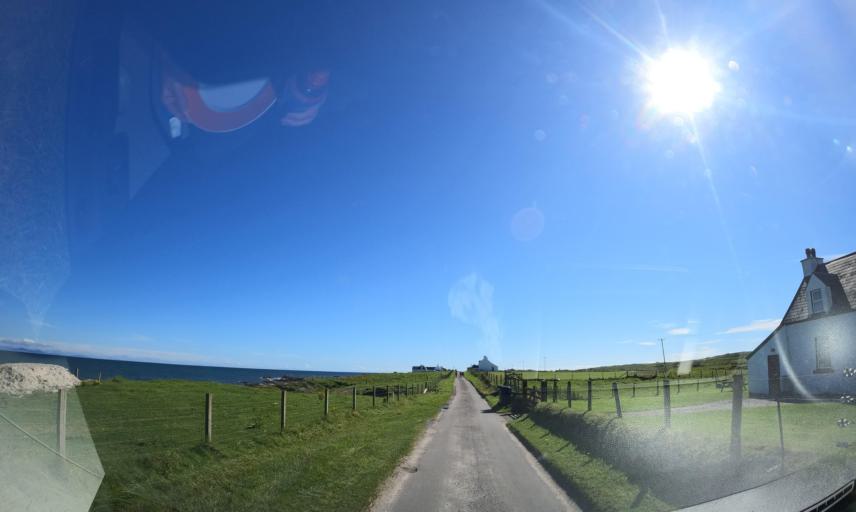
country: GB
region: Scotland
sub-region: Eilean Siar
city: Barra
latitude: 56.4636
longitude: -6.8944
